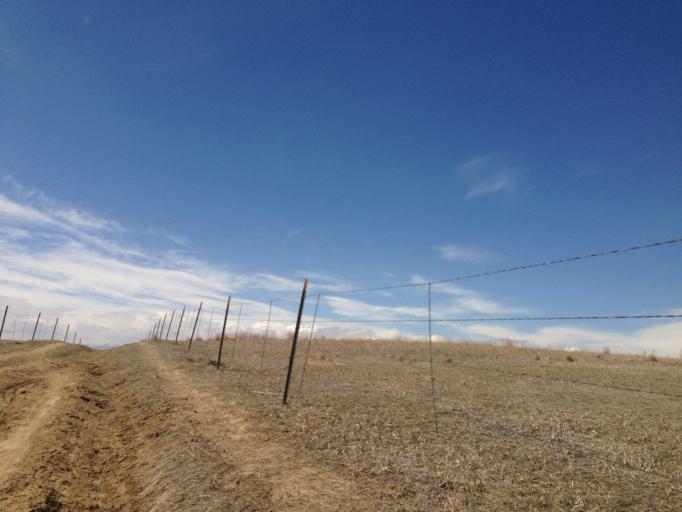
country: US
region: Colorado
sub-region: Boulder County
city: Gunbarrel
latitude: 40.0622
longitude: -105.1472
